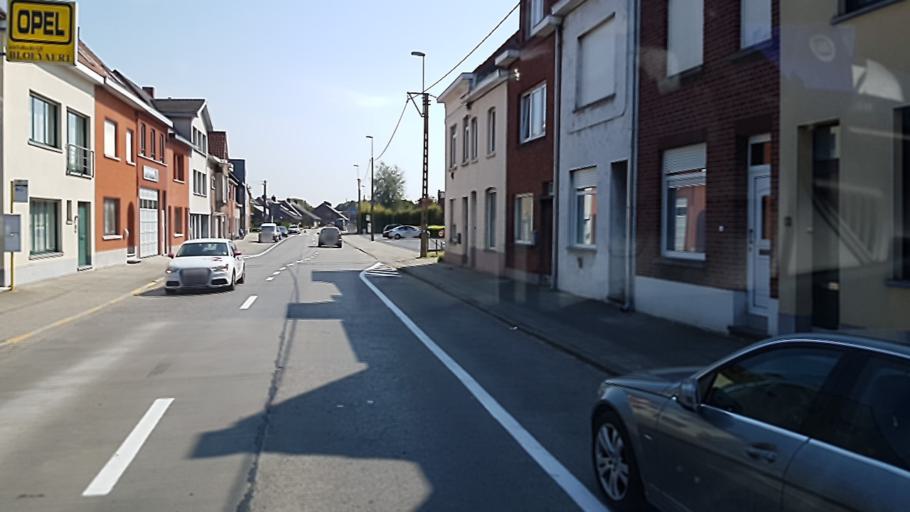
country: BE
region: Flanders
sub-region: Provincie West-Vlaanderen
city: Harelbeke
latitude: 50.8473
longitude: 3.3098
